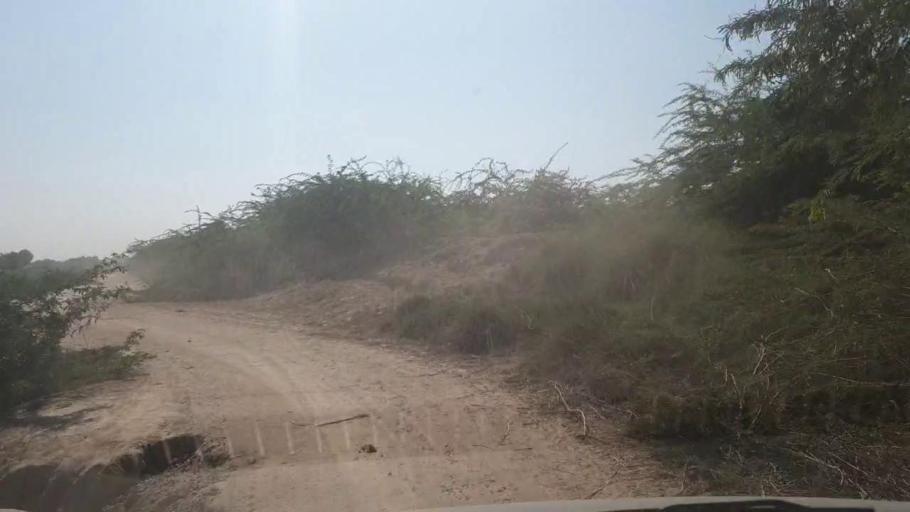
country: PK
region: Sindh
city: Tando Bago
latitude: 24.7707
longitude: 69.1550
